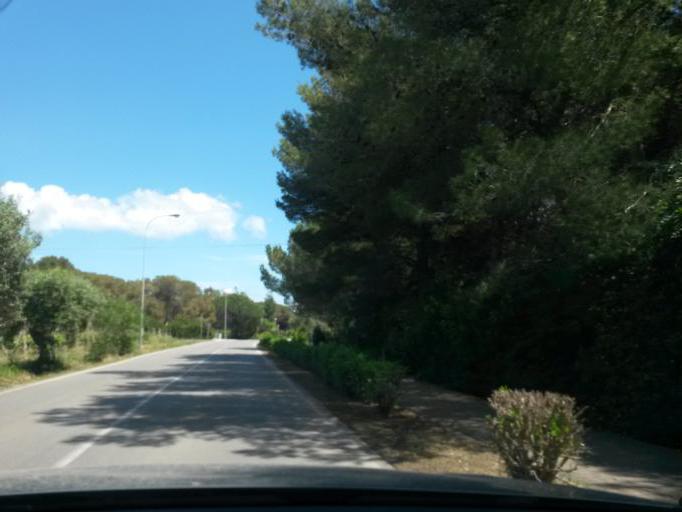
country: IT
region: Tuscany
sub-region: Provincia di Livorno
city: Portoferraio
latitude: 42.7619
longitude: 10.3058
